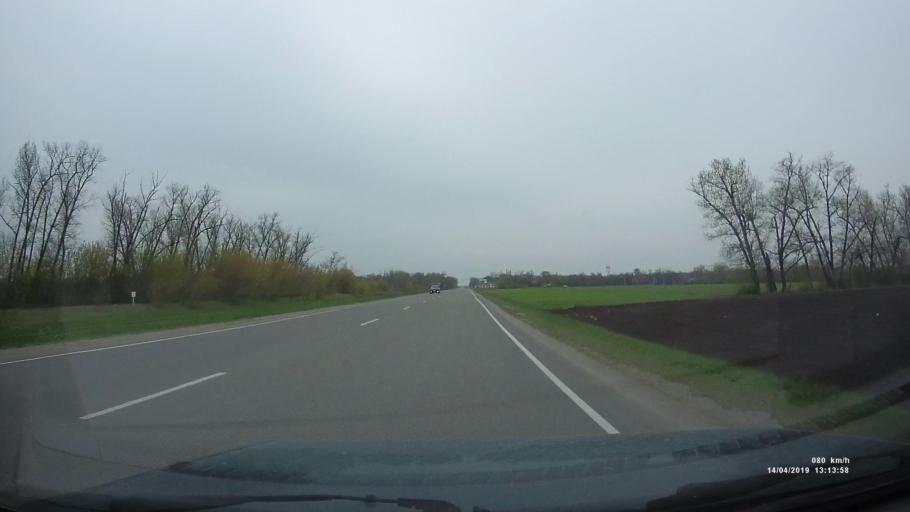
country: RU
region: Rostov
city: Kuleshovka
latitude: 47.0935
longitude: 39.6162
